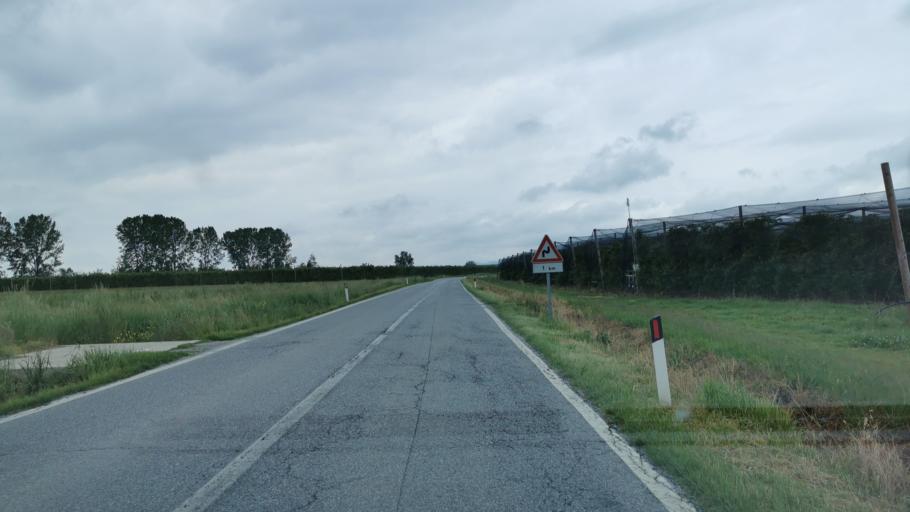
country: IT
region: Piedmont
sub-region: Provincia di Cuneo
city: Lagnasco
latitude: 44.5981
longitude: 7.5679
